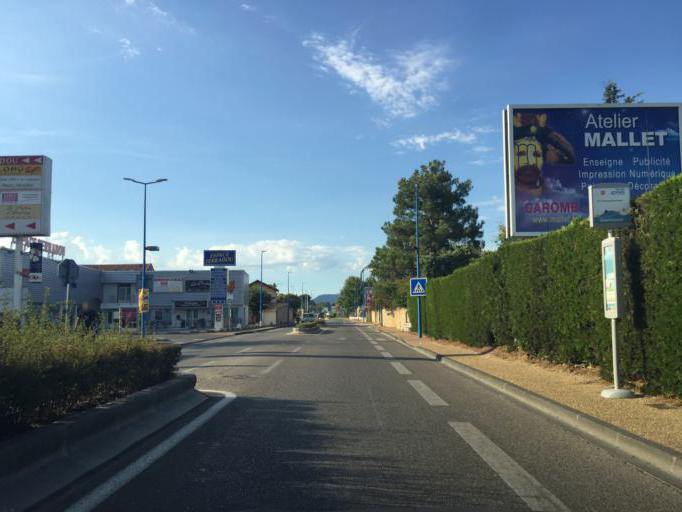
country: FR
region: Provence-Alpes-Cote d'Azur
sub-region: Departement du Vaucluse
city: Carpentras
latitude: 44.0353
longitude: 5.0511
